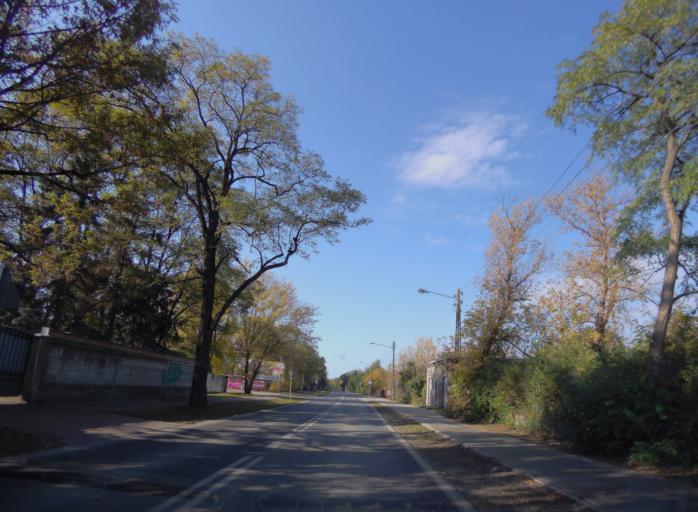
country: PL
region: Masovian Voivodeship
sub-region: Powiat otwocki
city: Jozefow
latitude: 52.1595
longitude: 21.2033
